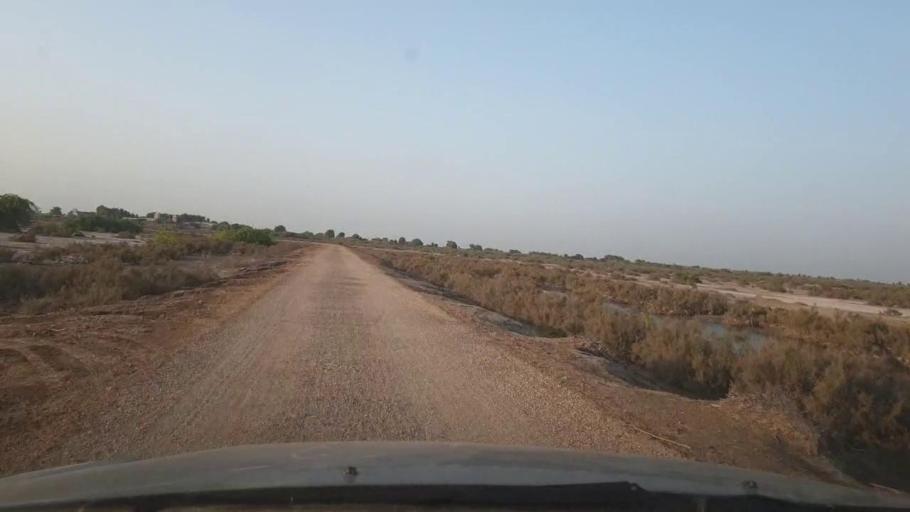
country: PK
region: Sindh
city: Tando Ghulam Ali
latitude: 25.1700
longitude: 68.9763
